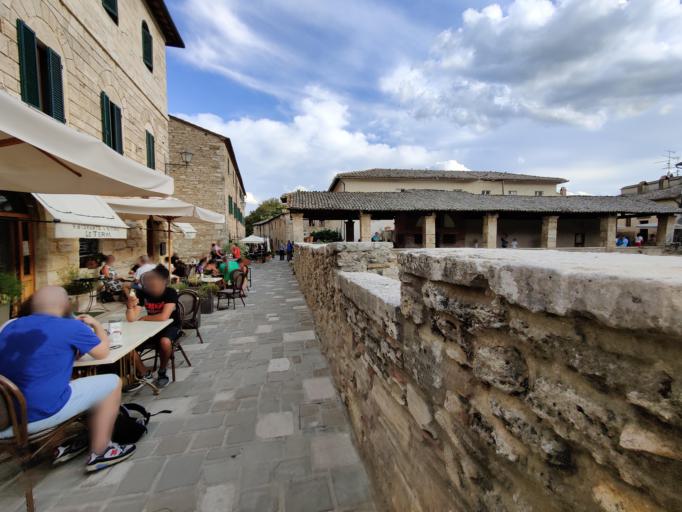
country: IT
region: Tuscany
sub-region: Provincia di Siena
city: Castiglione d'Orcia
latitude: 43.0285
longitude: 11.6180
